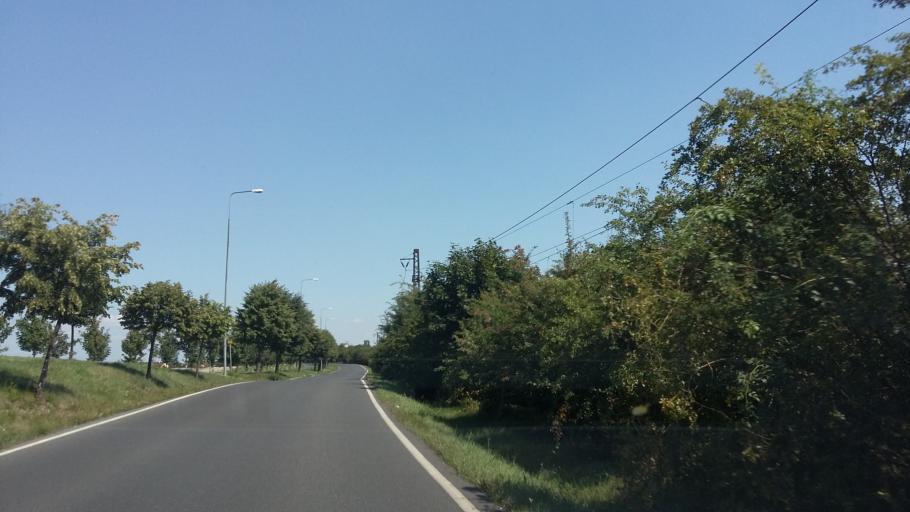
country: CZ
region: Central Bohemia
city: Zelenec
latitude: 50.1254
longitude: 14.6432
